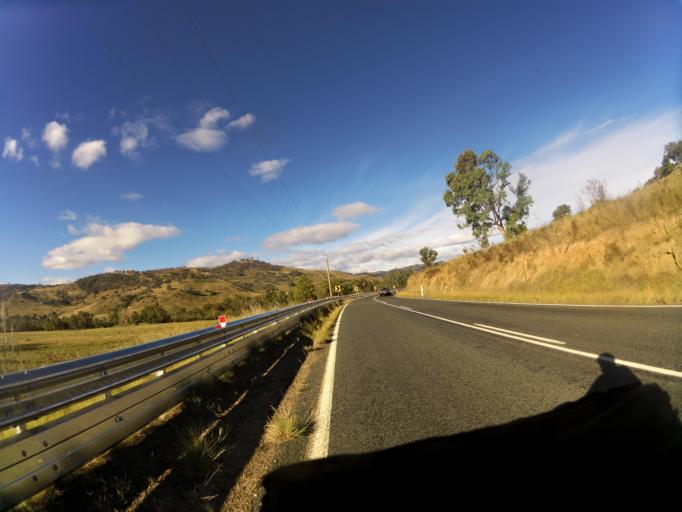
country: AU
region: New South Wales
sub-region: Greater Hume Shire
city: Holbrook
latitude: -35.9652
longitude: 147.7634
